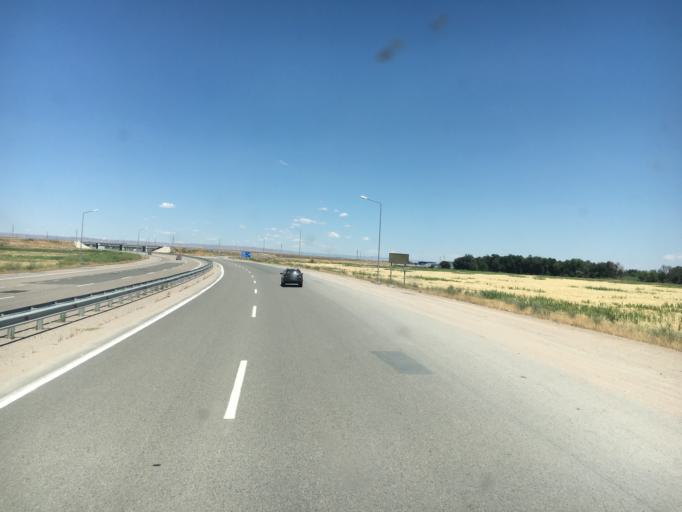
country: KG
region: Chuy
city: Sokuluk
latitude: 43.2702
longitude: 74.2253
